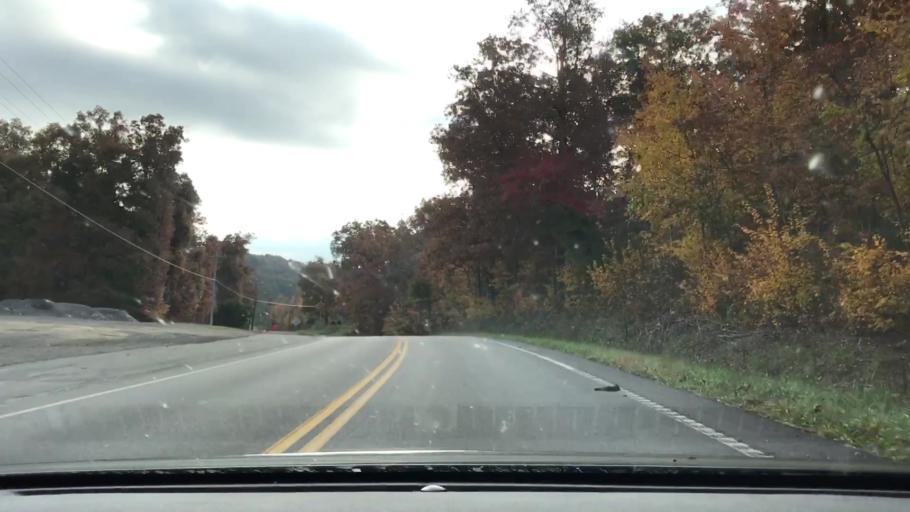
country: US
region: Tennessee
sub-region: Putnam County
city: Monterey
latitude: 36.1199
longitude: -85.1952
